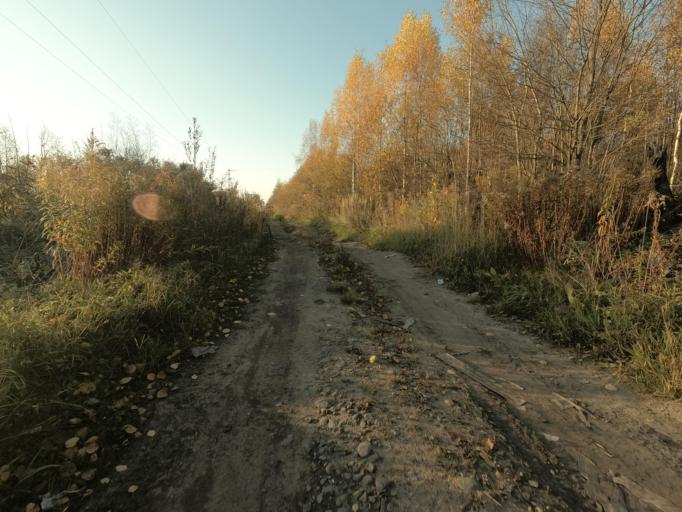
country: RU
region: Leningrad
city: Kirovsk
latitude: 59.8630
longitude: 31.0120
